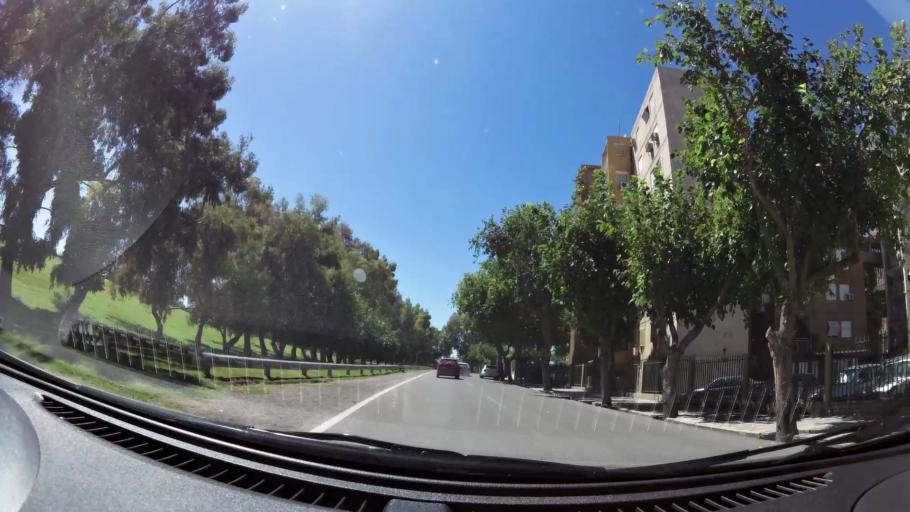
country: AR
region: San Juan
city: San Juan
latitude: -31.5190
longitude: -68.5327
